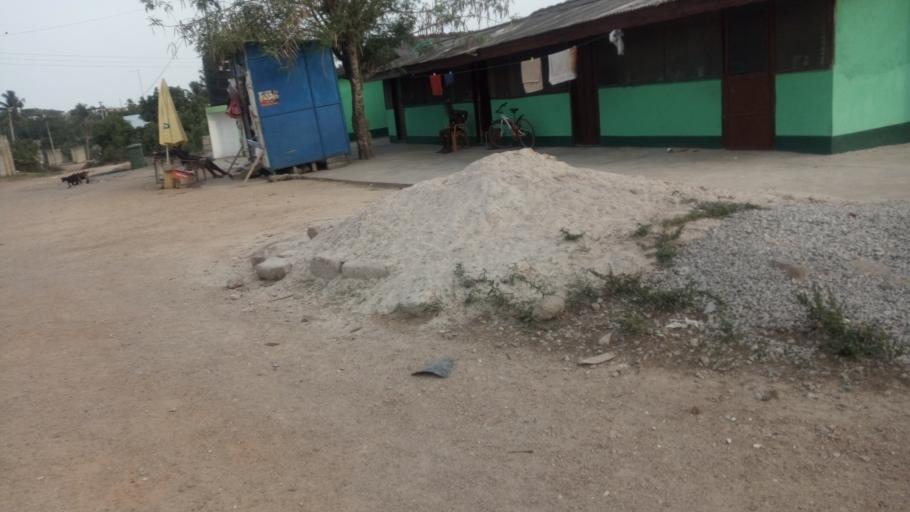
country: GH
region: Central
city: Winneba
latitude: 5.3555
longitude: -0.6244
